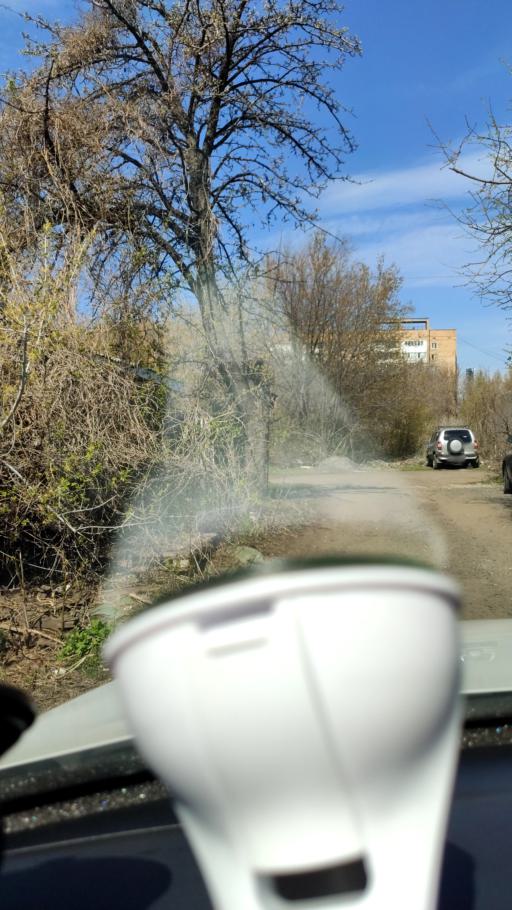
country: RU
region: Samara
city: Samara
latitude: 53.2328
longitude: 50.2314
